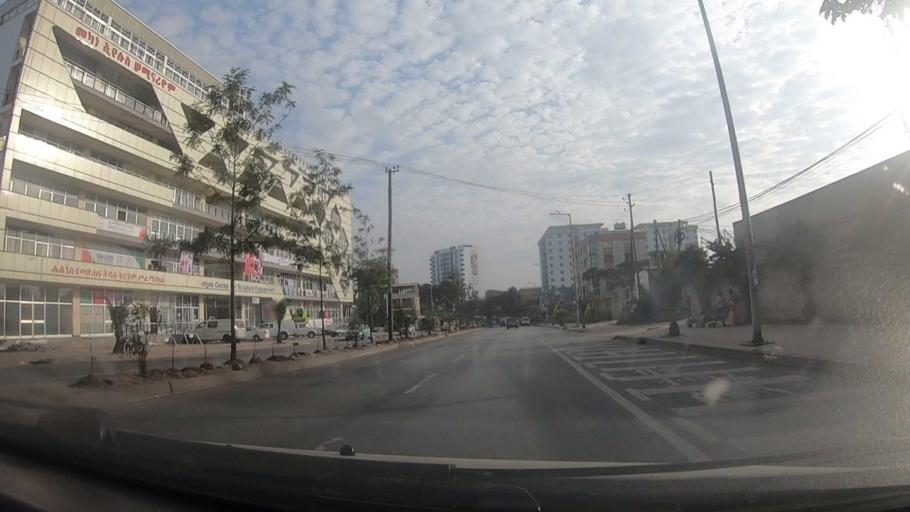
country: ET
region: Adis Abeba
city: Addis Ababa
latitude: 8.9704
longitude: 38.7313
